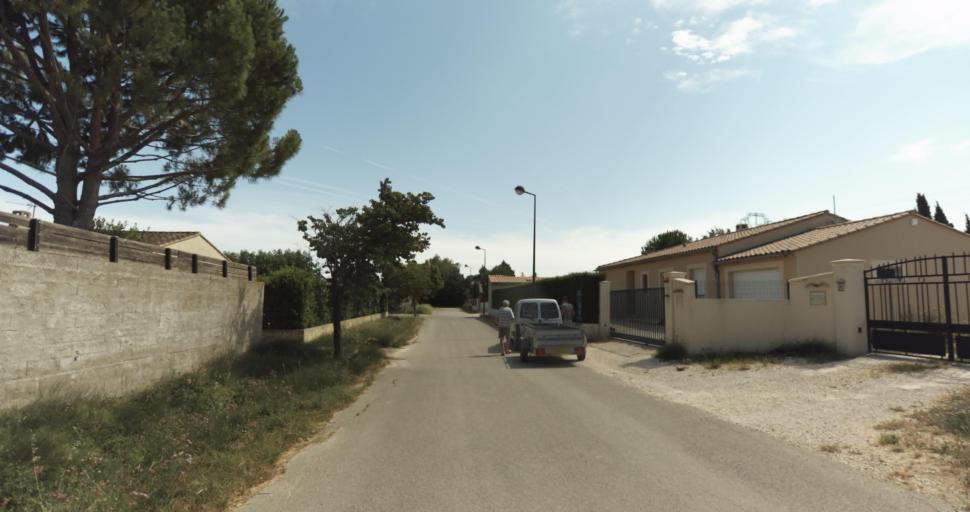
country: FR
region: Provence-Alpes-Cote d'Azur
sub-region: Departement du Vaucluse
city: Monteux
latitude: 44.0340
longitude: 4.9787
